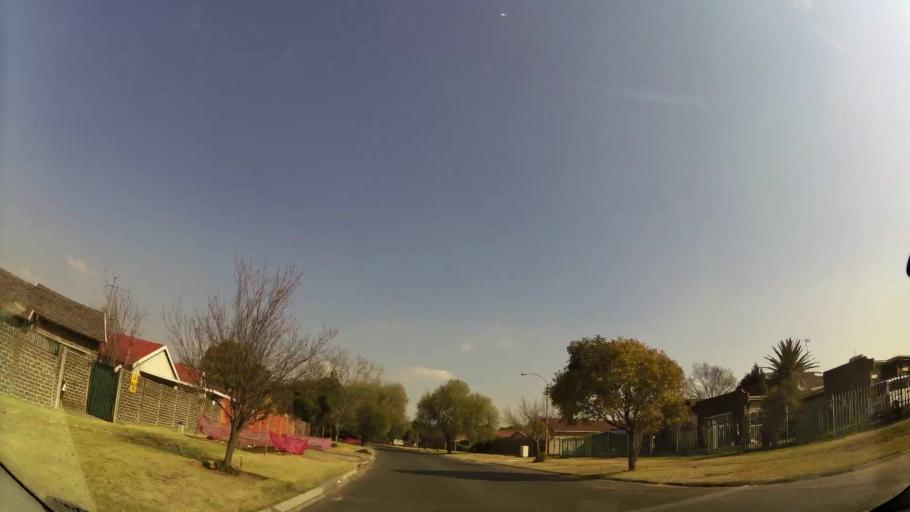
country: ZA
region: Gauteng
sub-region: Ekurhuleni Metropolitan Municipality
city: Benoni
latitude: -26.1488
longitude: 28.2842
